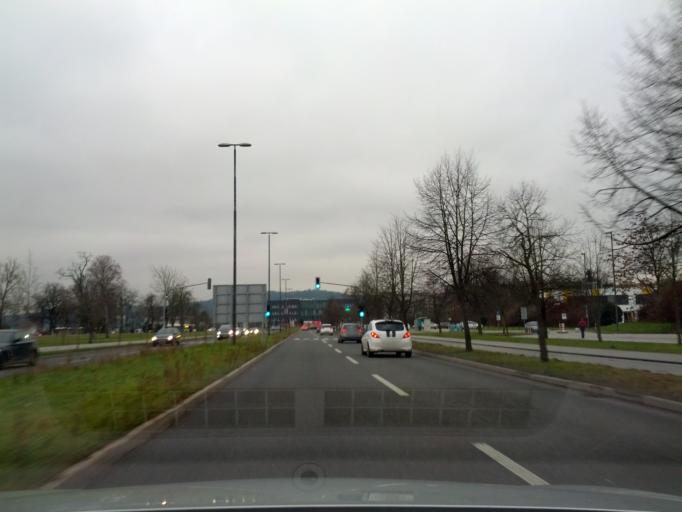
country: SI
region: Ljubljana
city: Ljubljana
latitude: 46.0690
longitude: 14.5260
